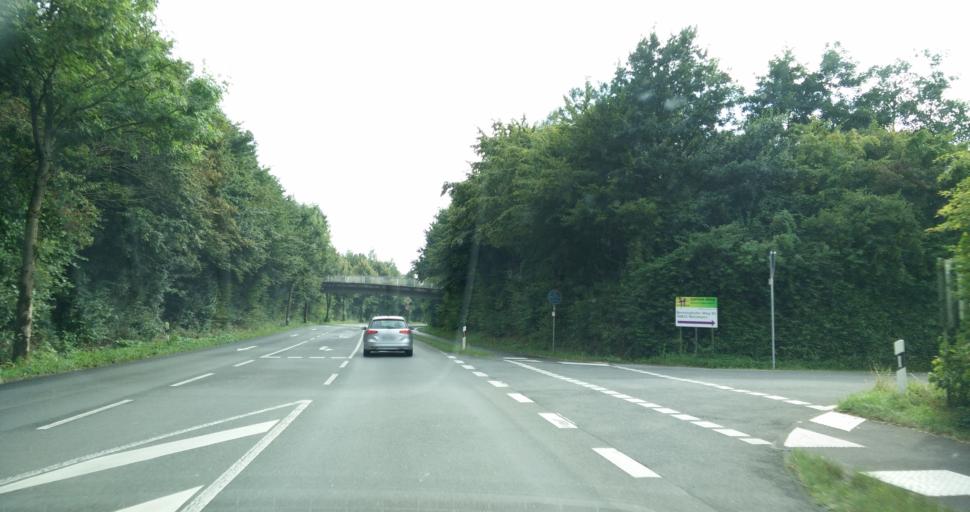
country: DE
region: North Rhine-Westphalia
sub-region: Regierungsbezirk Dusseldorf
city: Mettmann
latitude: 51.2385
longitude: 7.0043
